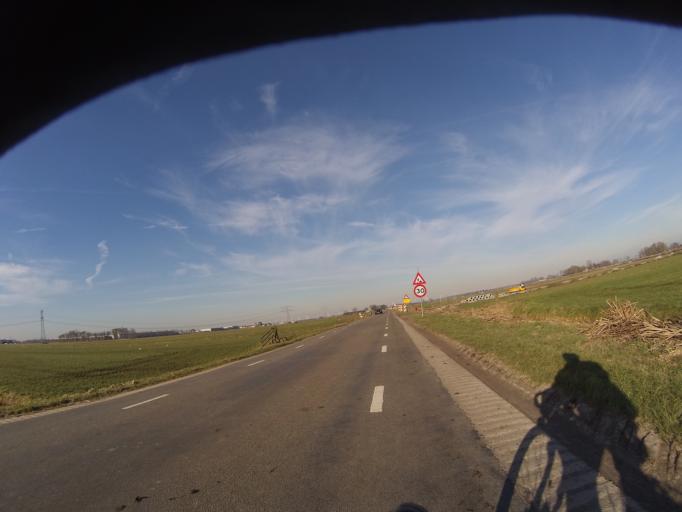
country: NL
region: Utrecht
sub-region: Gemeente Bunschoten
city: Bunschoten
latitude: 52.2197
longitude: 5.3900
